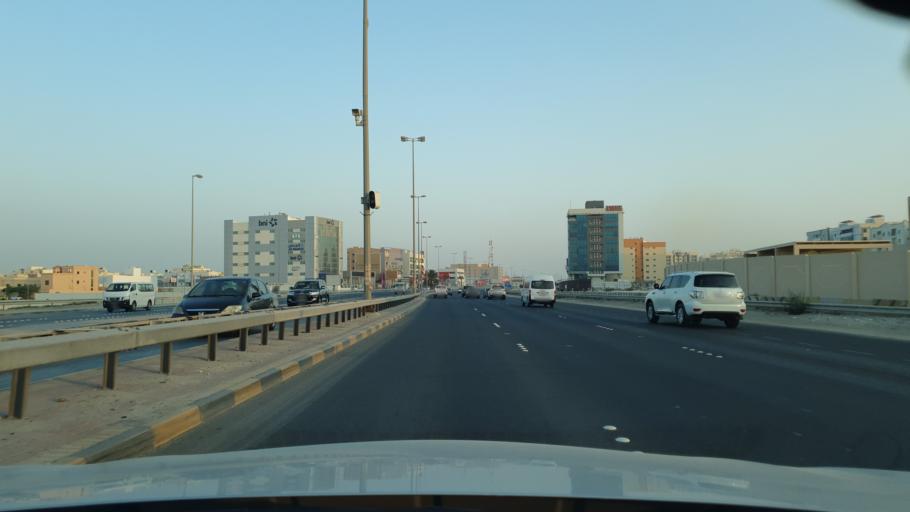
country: BH
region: Northern
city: Ar Rifa'
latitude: 26.1405
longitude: 50.5810
